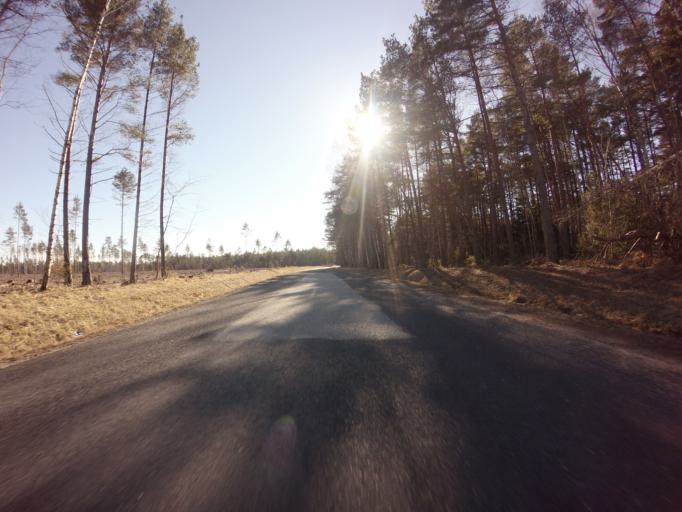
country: EE
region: Saare
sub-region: Kuressaare linn
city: Kuressaare
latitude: 58.5908
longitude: 22.5747
